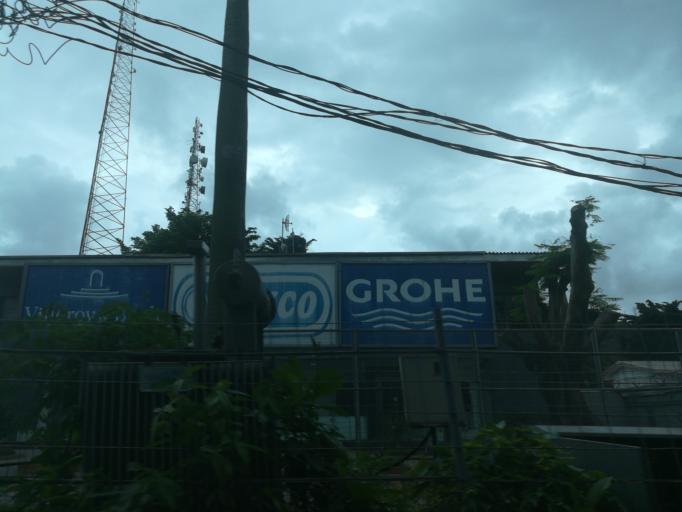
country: NG
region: Lagos
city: Ikoyi
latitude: 6.4281
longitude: 3.4212
